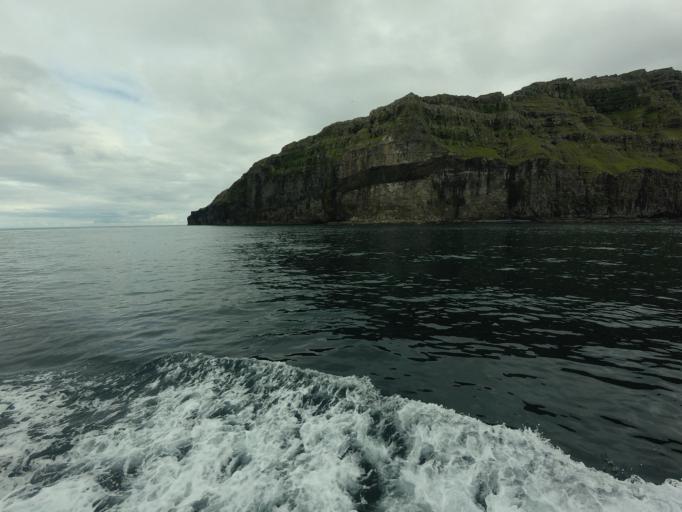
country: FO
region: Nordoyar
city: Klaksvik
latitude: 62.3071
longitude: -6.3502
